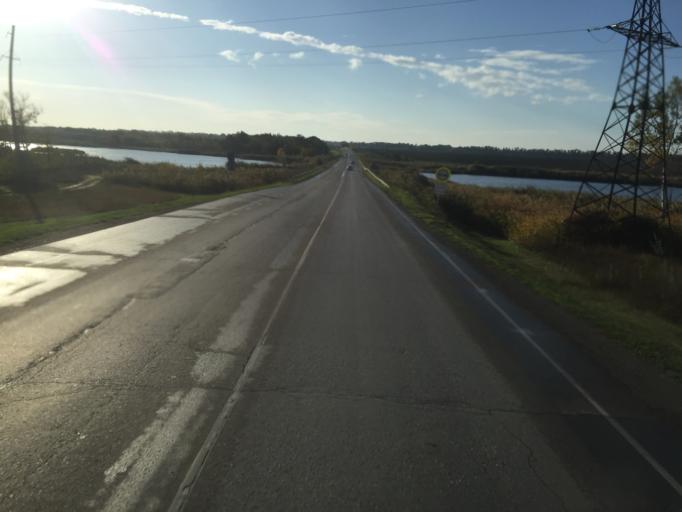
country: RU
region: Rostov
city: Mechetinskaya
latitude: 46.7719
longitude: 40.4218
